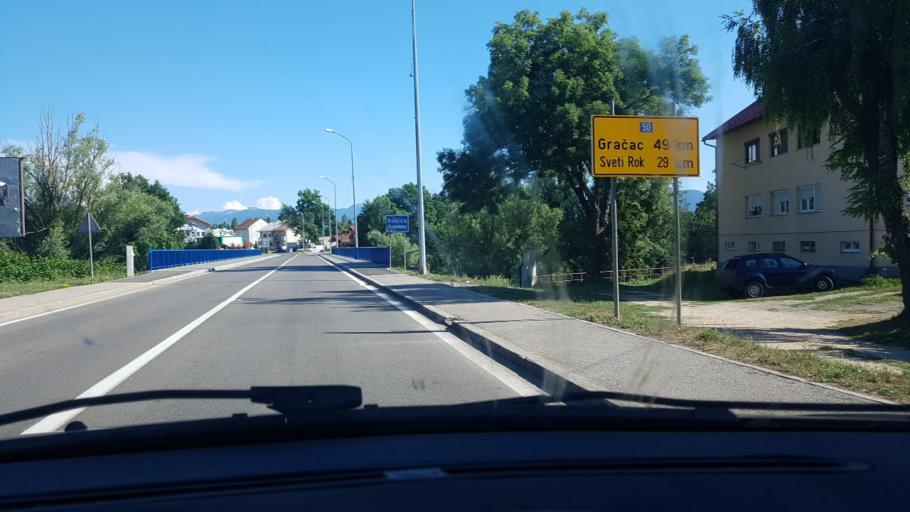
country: HR
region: Licko-Senjska
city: Gospic
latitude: 44.5440
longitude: 15.3734
